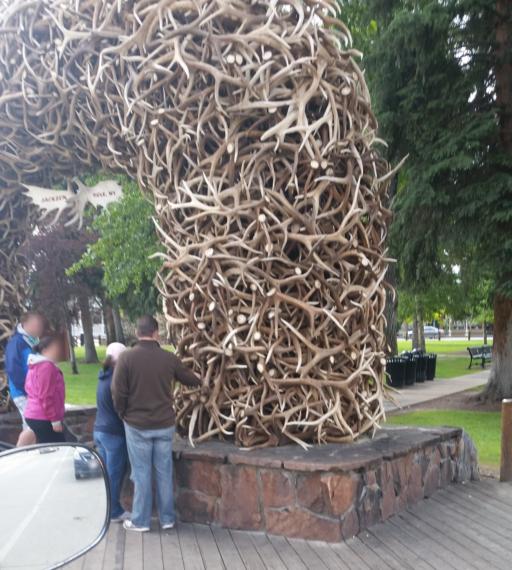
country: US
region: Wyoming
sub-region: Teton County
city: Jackson
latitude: 43.4796
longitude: -110.7625
